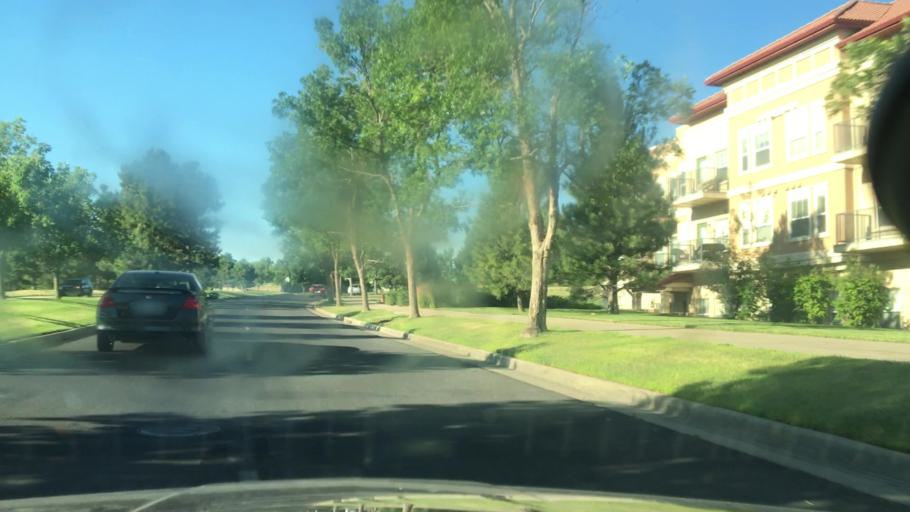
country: US
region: Colorado
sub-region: Arapahoe County
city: Castlewood
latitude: 39.6168
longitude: -104.8855
